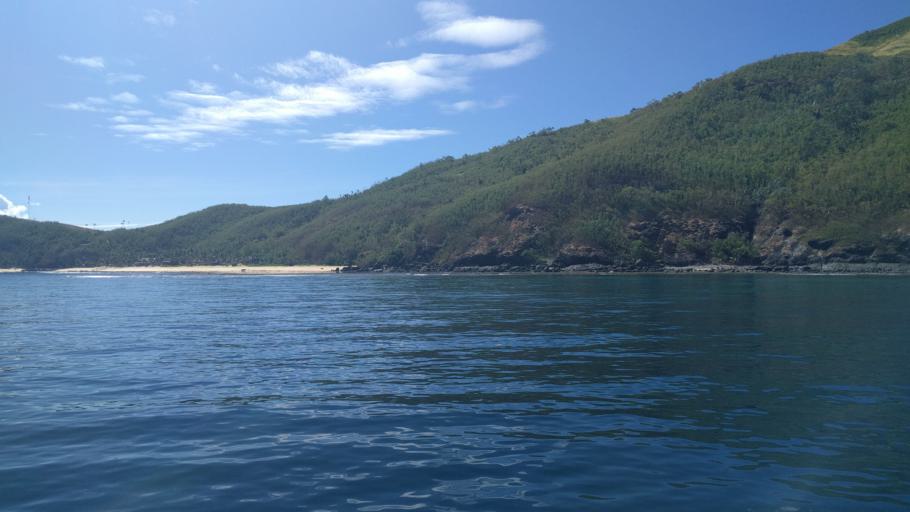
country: FJ
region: Western
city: Lautoka
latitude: -17.2816
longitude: 177.1032
